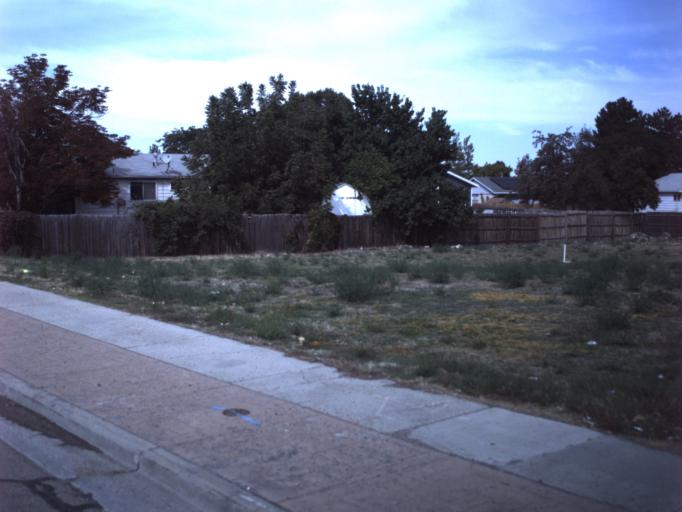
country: US
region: Utah
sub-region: Salt Lake County
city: Kearns
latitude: 40.6532
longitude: -111.9676
